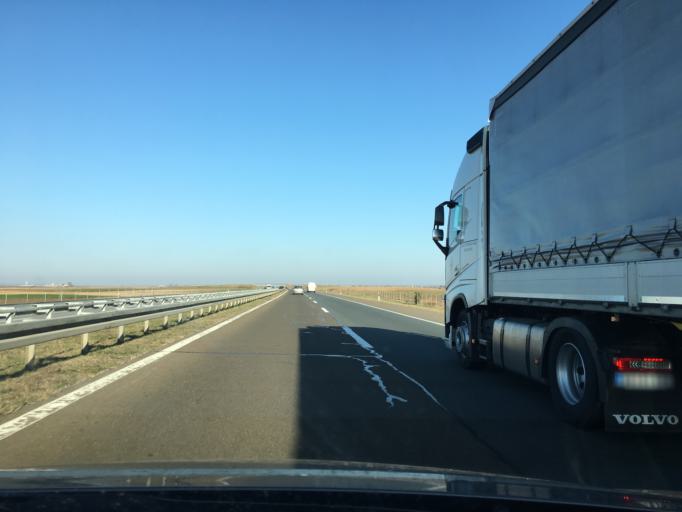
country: RS
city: Novi Karlovci
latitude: 45.0398
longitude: 20.1822
